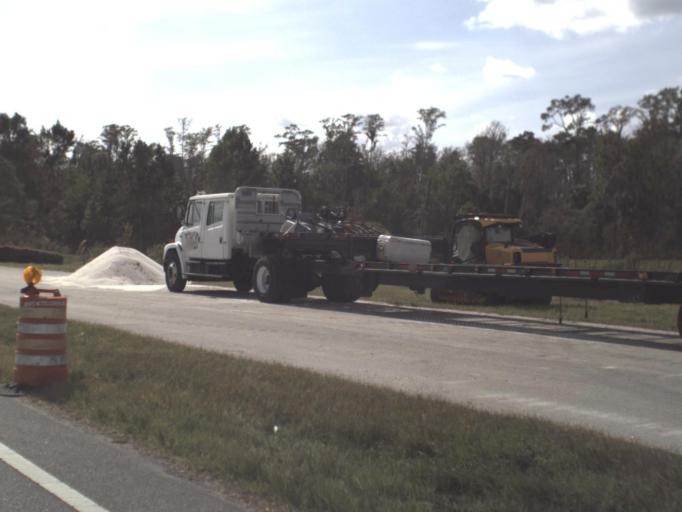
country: US
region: Florida
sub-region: Osceola County
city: Campbell
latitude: 28.3008
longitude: -81.4766
